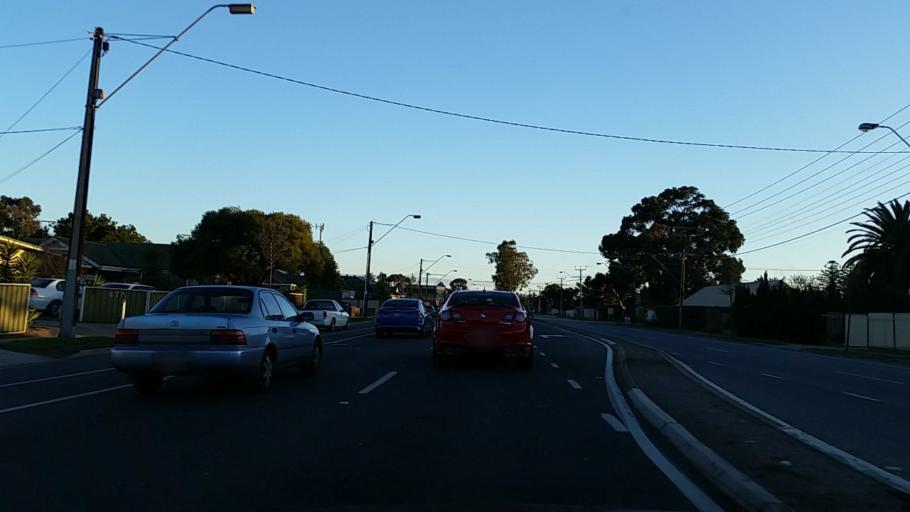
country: AU
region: South Australia
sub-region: Salisbury
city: Salisbury
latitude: -34.7890
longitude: 138.6176
